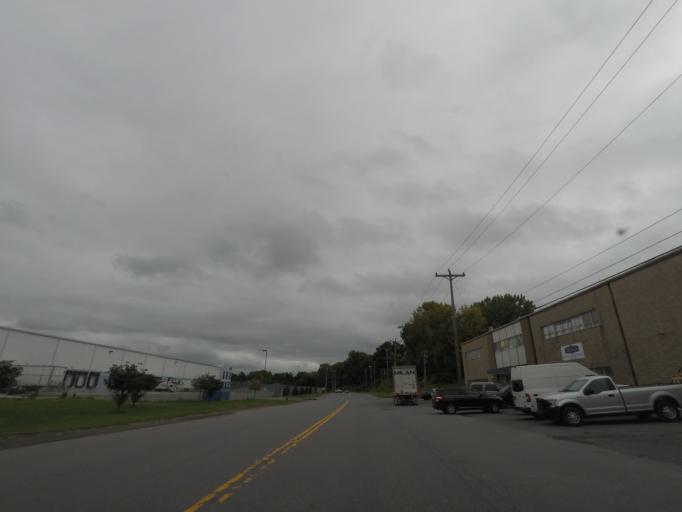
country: US
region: New York
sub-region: Albany County
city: West Albany
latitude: 42.6770
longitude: -73.7772
